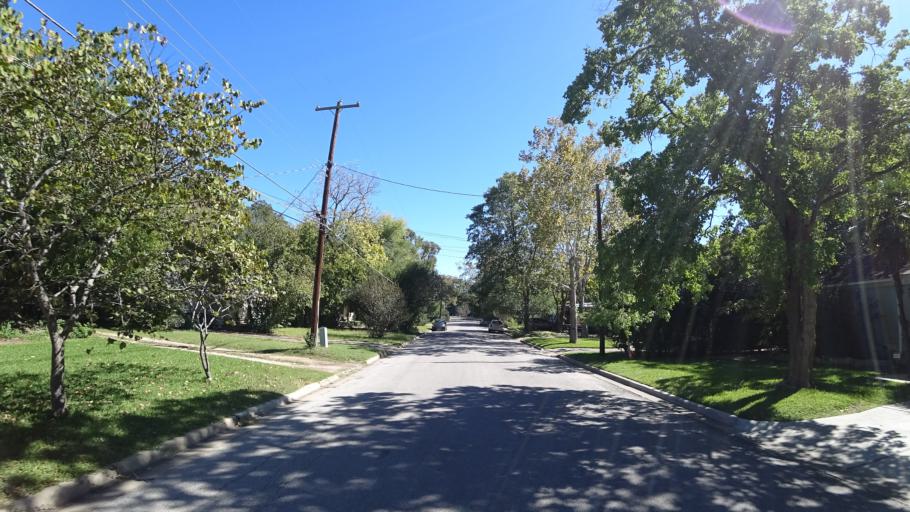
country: US
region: Texas
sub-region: Travis County
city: Austin
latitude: 30.3351
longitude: -97.7345
